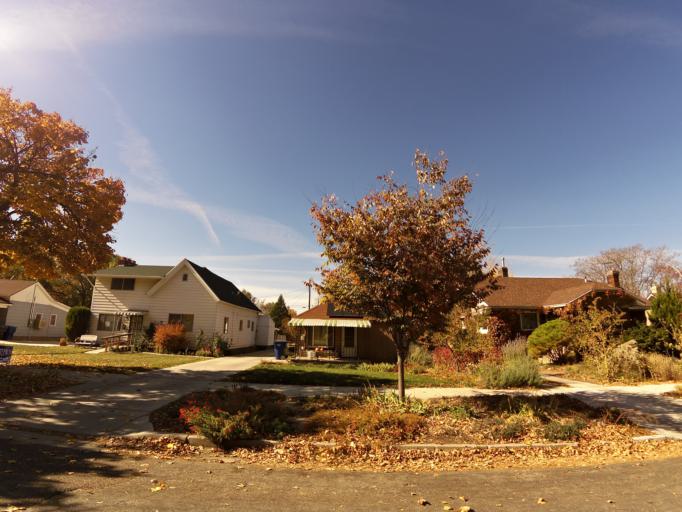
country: US
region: Utah
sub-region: Weber County
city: Ogden
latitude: 41.2305
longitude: -111.9620
